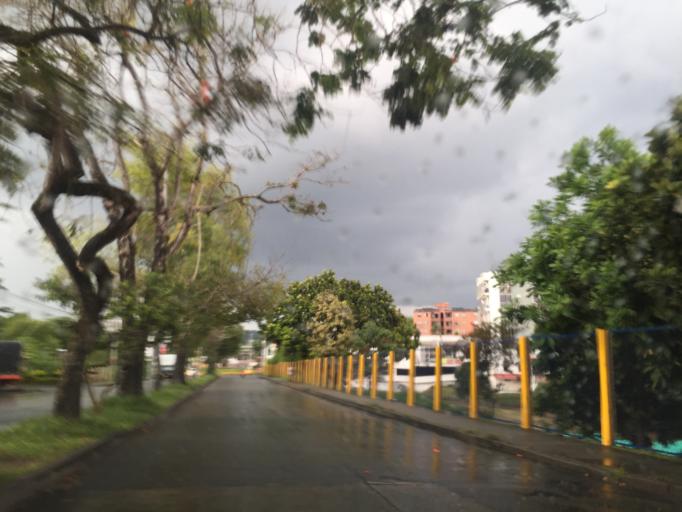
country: CO
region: Quindio
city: Armenia
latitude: 4.5454
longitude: -75.6661
